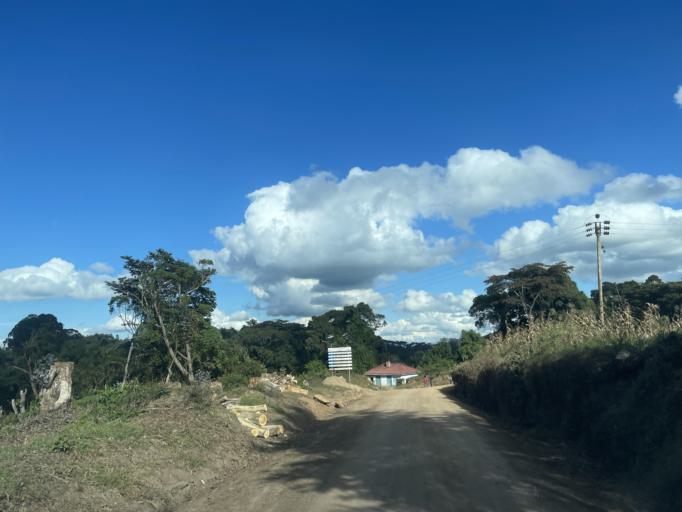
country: TZ
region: Iringa
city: Makungu
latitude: -8.4785
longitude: 35.4205
